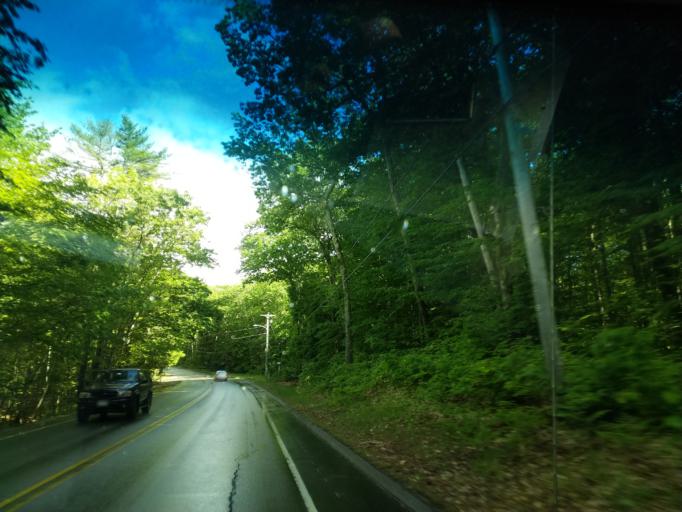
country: US
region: Maine
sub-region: Cumberland County
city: Cumberland Center
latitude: 43.7490
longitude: -70.3126
